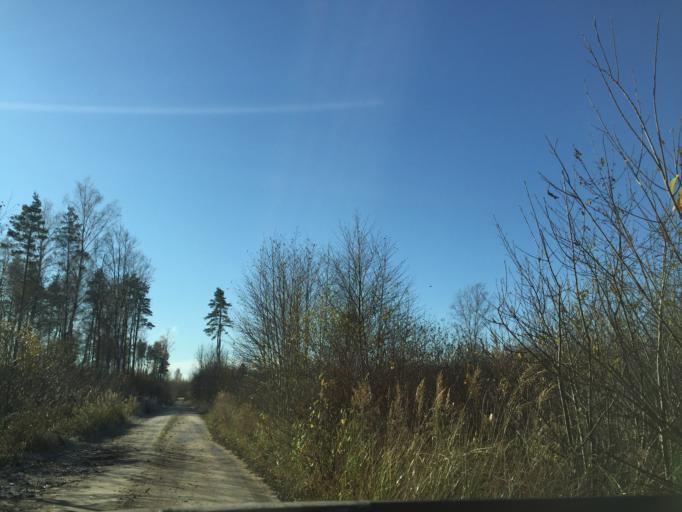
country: LV
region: Aizkraukles Rajons
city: Aizkraukle
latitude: 56.7176
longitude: 25.3006
